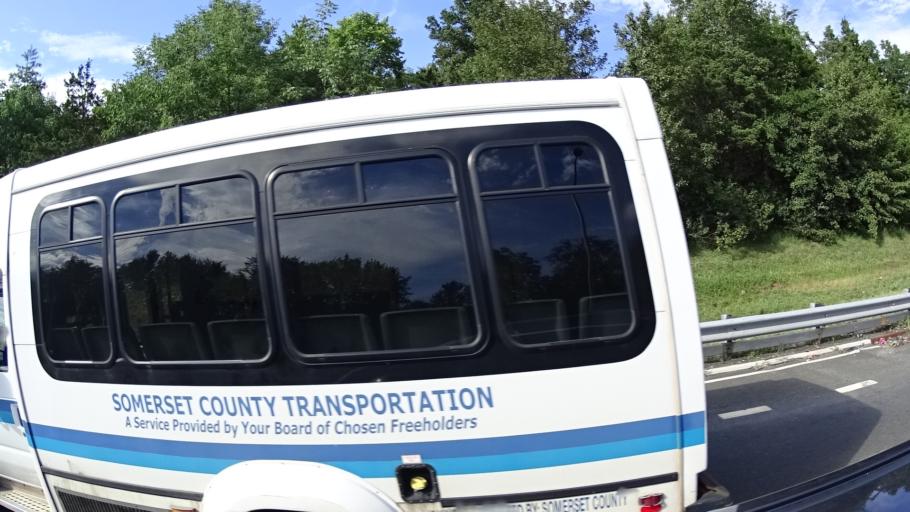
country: US
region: New Jersey
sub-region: Somerset County
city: Somerville
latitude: 40.5822
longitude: -74.6210
